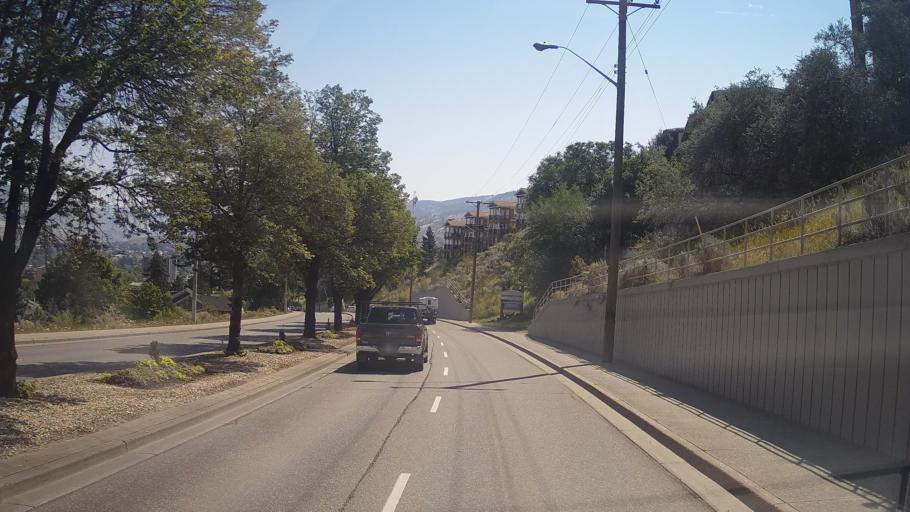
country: CA
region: British Columbia
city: Kamloops
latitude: 50.6718
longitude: -120.3432
